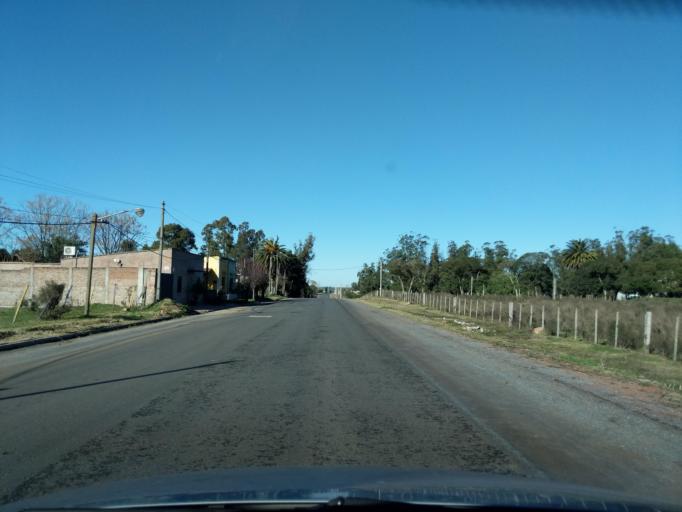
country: UY
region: Florida
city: Florida
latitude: -34.0935
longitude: -56.2393
